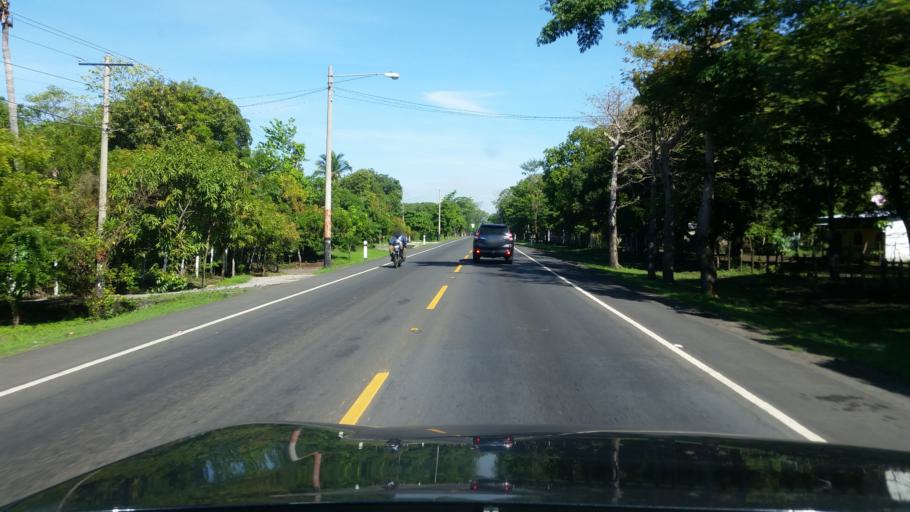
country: NI
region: Chinandega
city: Chichigalpa
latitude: 12.6084
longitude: -87.0703
